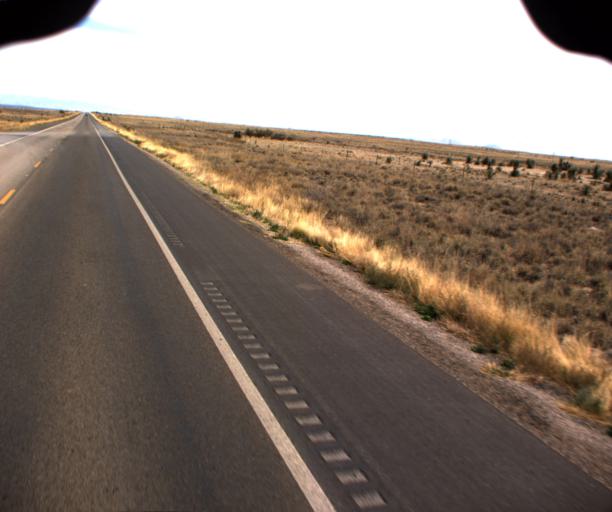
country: US
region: Arizona
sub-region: Cochise County
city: Willcox
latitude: 32.2399
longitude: -109.8123
